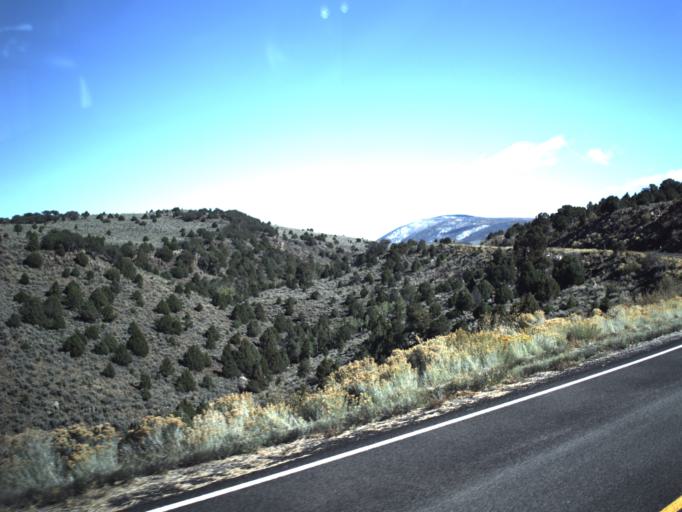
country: US
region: Utah
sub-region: Wayne County
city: Loa
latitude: 38.4796
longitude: -111.8264
